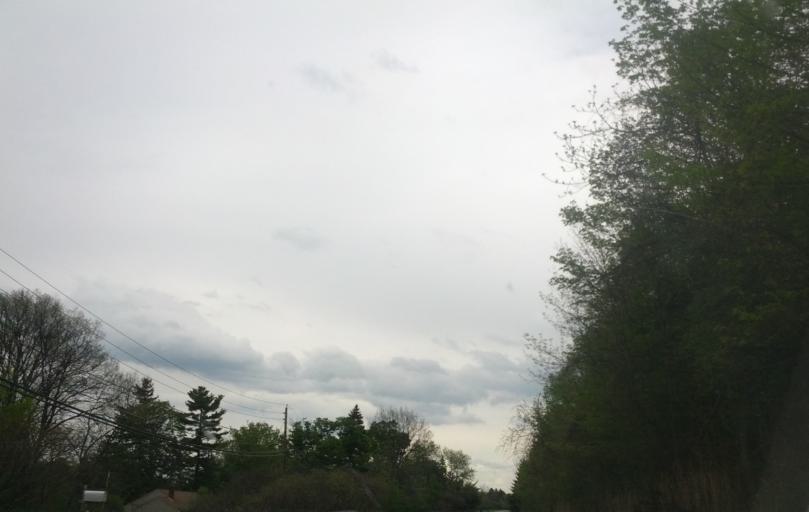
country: US
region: New York
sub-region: Onondaga County
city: Nedrow
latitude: 42.9958
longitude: -76.1054
